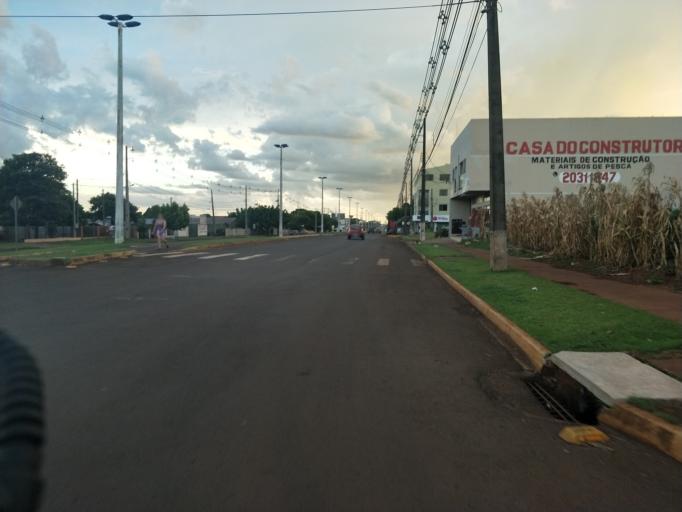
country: BR
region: Parana
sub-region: Marechal Candido Rondon
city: Marechal Candido Rondon
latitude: -24.5499
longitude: -54.0456
